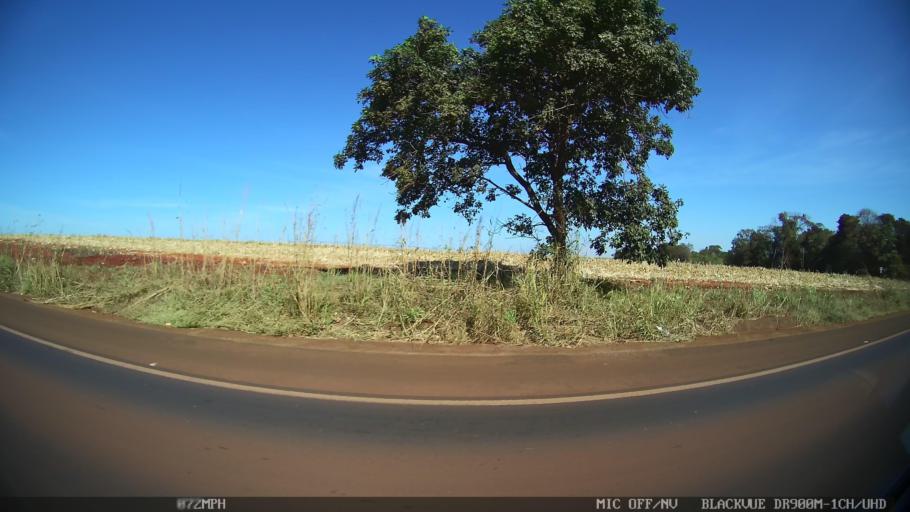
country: BR
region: Sao Paulo
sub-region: Guaira
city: Guaira
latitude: -20.4443
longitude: -48.3614
